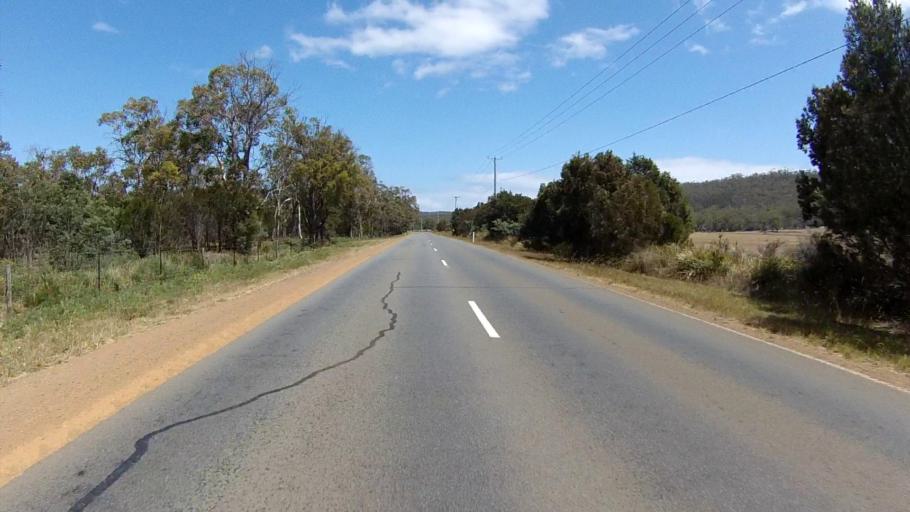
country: AU
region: Tasmania
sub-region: Clarence
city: Sandford
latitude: -42.9418
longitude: 147.4871
